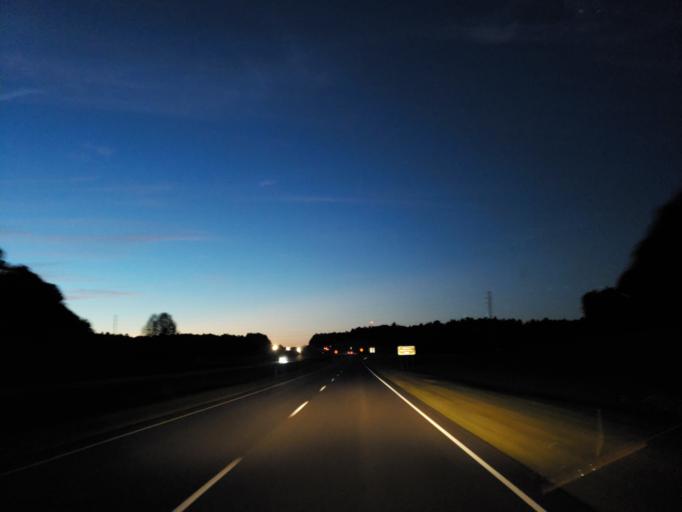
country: US
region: Mississippi
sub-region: Clarke County
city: Quitman
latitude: 32.0994
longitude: -88.7053
